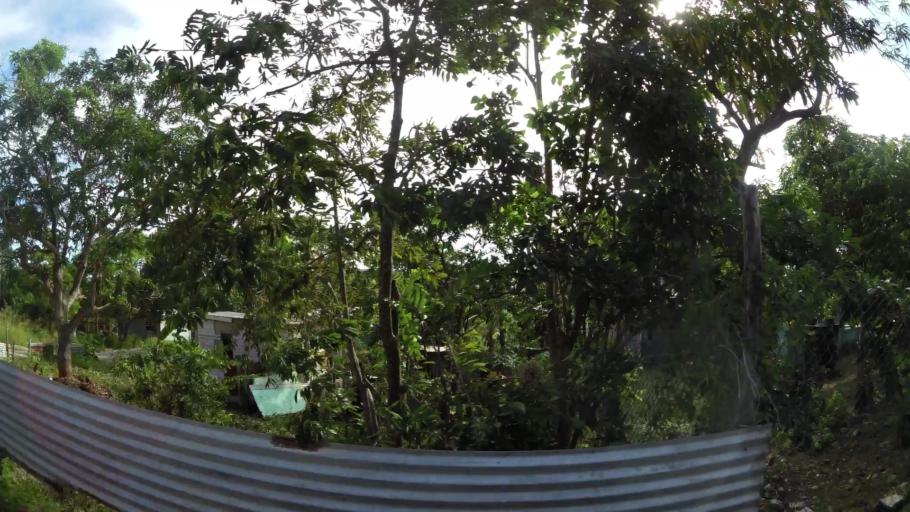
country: AG
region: Saint Peter
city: All Saints
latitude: 17.0536
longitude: -61.8001
